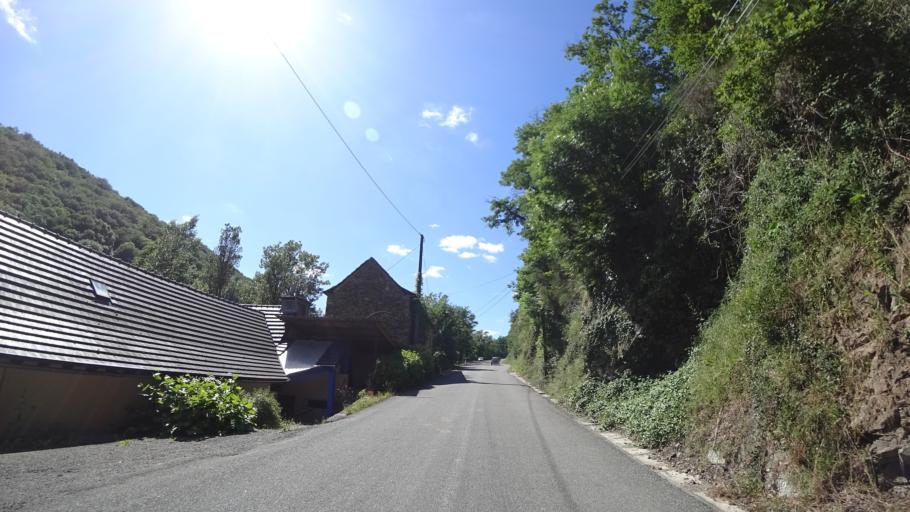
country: FR
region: Midi-Pyrenees
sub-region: Departement de l'Aveyron
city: Colombies
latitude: 44.3773
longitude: 2.3099
